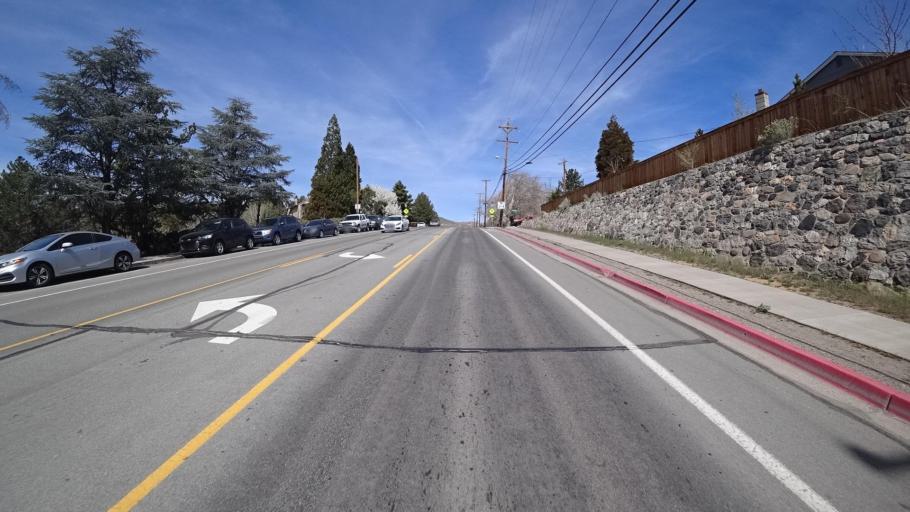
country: US
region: Nevada
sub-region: Washoe County
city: Reno
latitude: 39.5420
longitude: -119.8203
